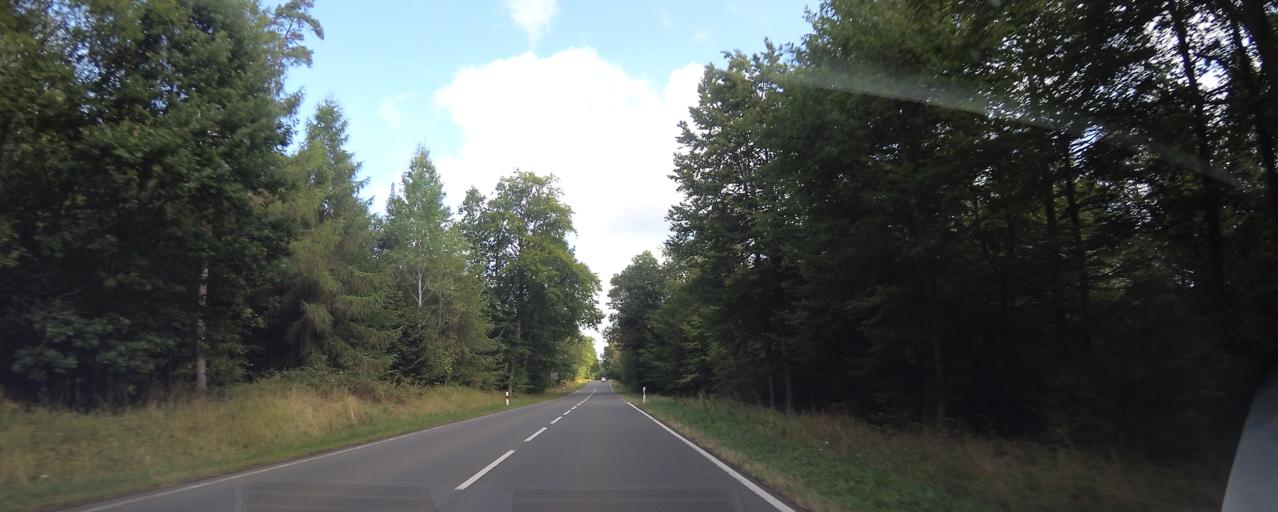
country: DE
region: Rheinland-Pfalz
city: Zemmer
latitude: 49.9163
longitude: 6.7066
